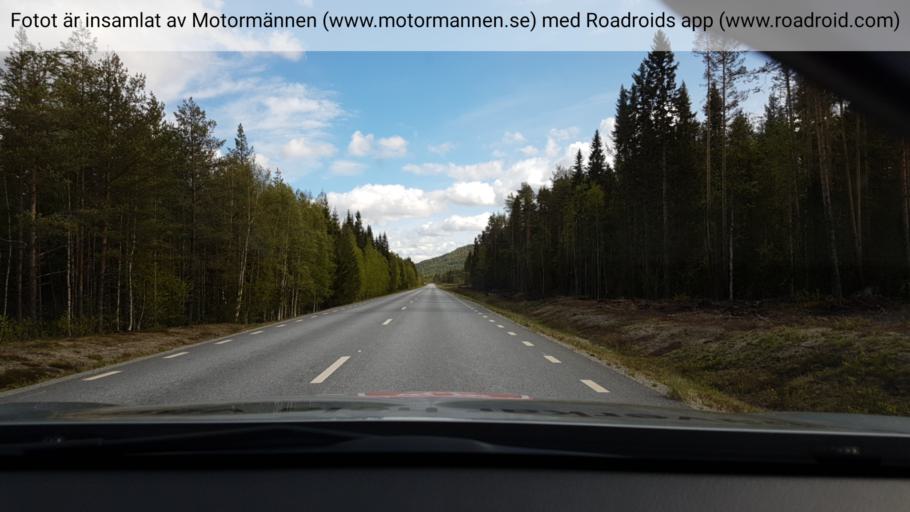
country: SE
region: Vaesterbotten
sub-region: Asele Kommun
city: Insjon
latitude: 64.1880
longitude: 17.7796
